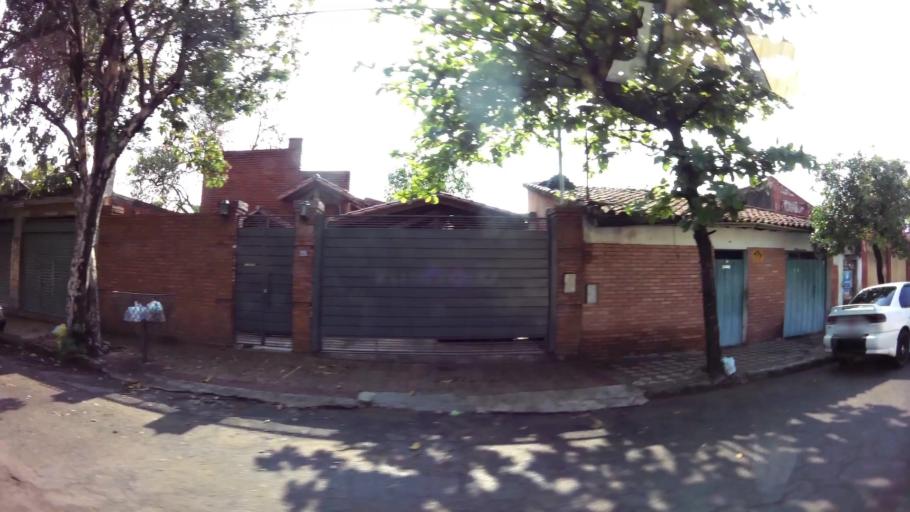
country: PY
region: Presidente Hayes
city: Nanawa
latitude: -25.2789
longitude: -57.6553
